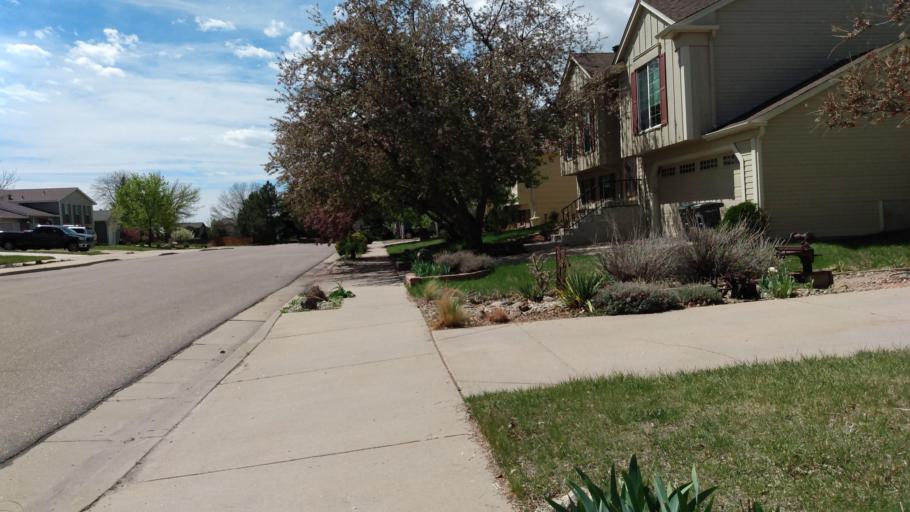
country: US
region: Colorado
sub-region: Boulder County
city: Lafayette
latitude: 40.0093
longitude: -105.0968
